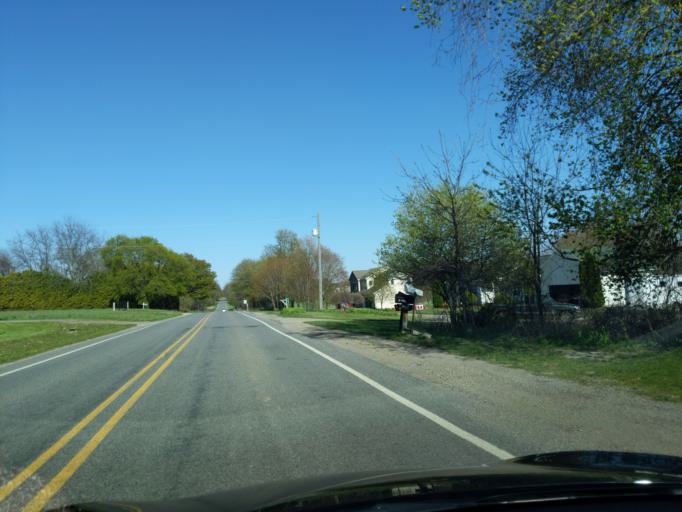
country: US
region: Michigan
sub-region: Kent County
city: Lowell
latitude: 42.8859
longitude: -85.3113
